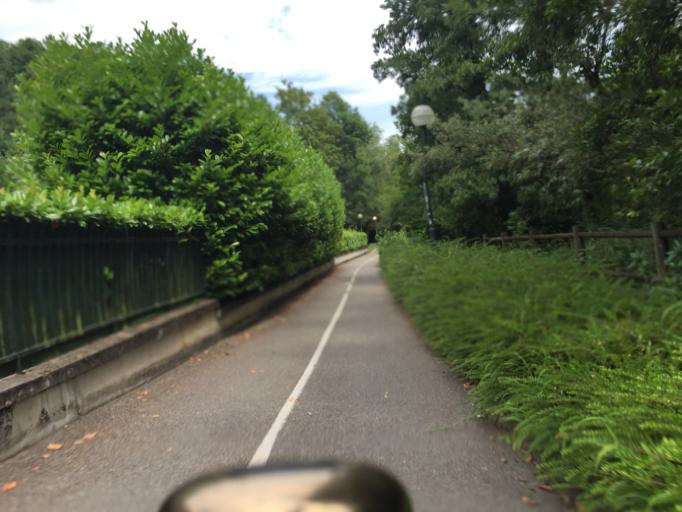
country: FR
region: Rhone-Alpes
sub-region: Departement de la Savoie
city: Le Bourget-du-Lac
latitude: 45.6499
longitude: 5.8619
